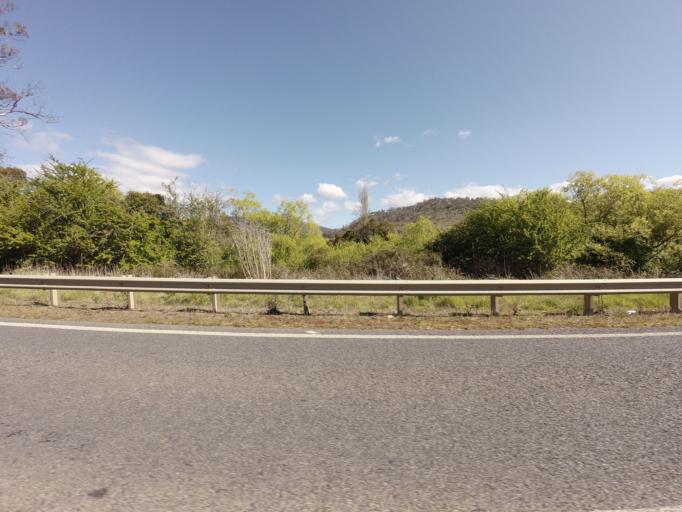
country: AU
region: Tasmania
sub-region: Derwent Valley
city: New Norfolk
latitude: -42.7642
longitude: 147.0176
